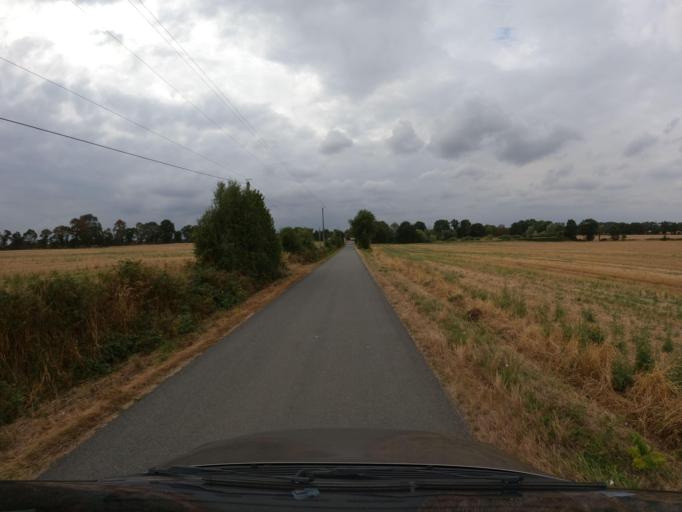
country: FR
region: Pays de la Loire
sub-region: Departement de Maine-et-Loire
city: La Romagne
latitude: 47.0516
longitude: -1.0050
